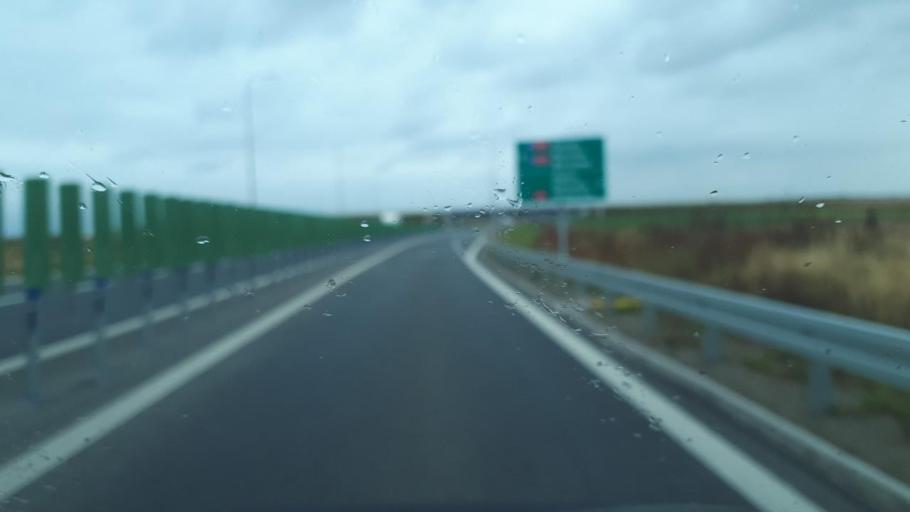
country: PL
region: Greater Poland Voivodeship
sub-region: Powiat kepinski
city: Baranow
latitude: 51.2533
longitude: 18.0157
